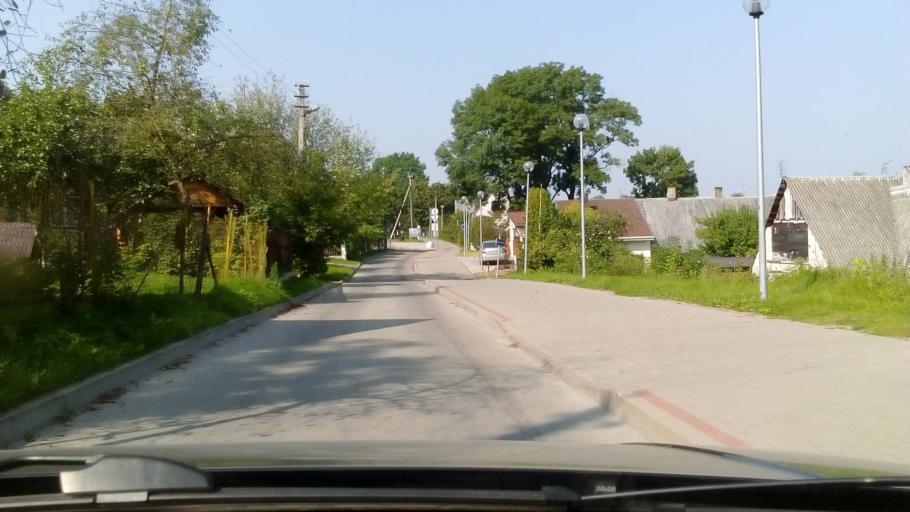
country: LT
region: Alytaus apskritis
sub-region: Alytus
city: Alytus
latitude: 54.4010
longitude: 24.0521
